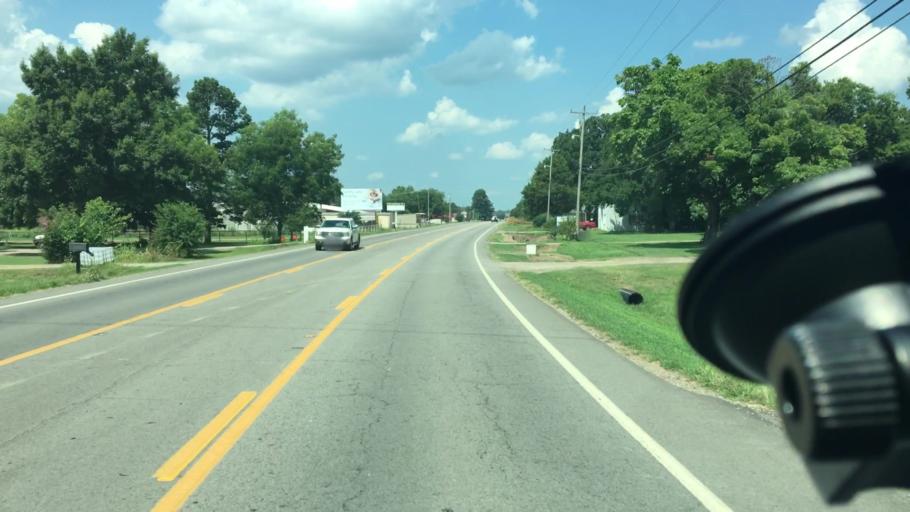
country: US
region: Arkansas
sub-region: Logan County
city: Paris
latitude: 35.2920
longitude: -93.7078
